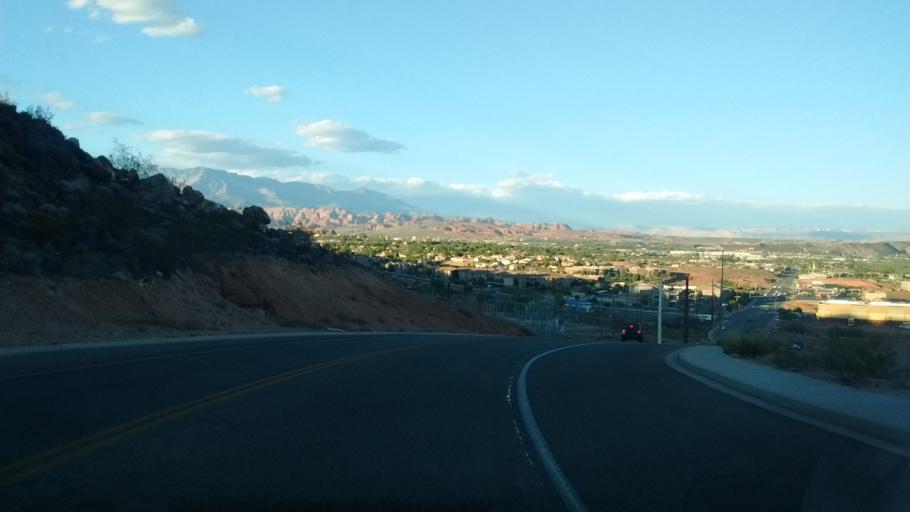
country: US
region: Utah
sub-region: Washington County
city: Saint George
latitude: 37.0954
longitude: -113.5443
